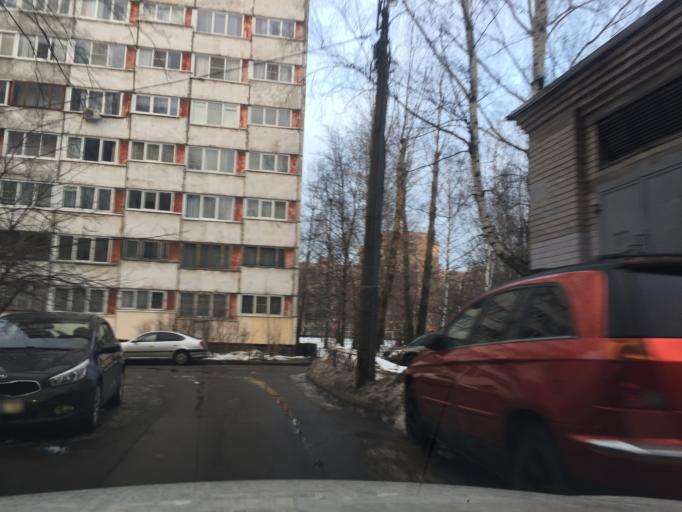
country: RU
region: St.-Petersburg
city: Grazhdanka
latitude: 60.0336
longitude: 30.4093
